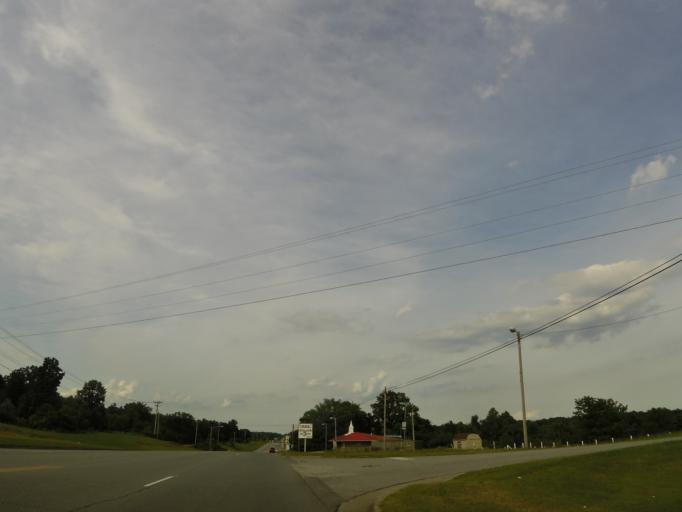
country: US
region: Tennessee
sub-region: Humphreys County
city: New Johnsonville
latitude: 36.0254
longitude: -87.9582
